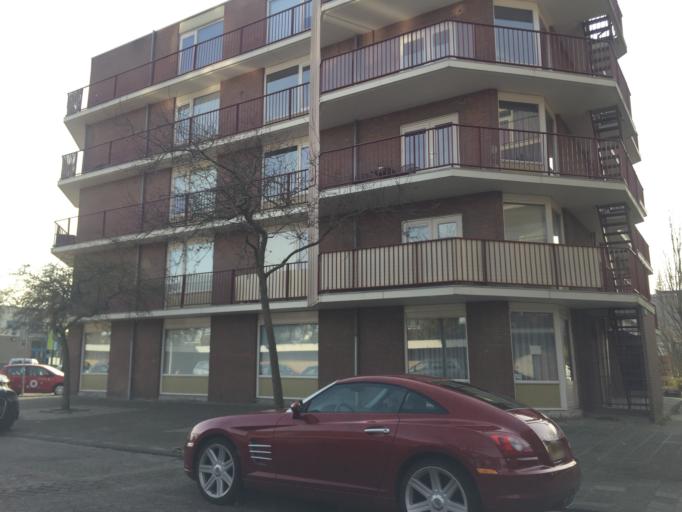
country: NL
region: South Holland
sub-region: Gemeente Leiden
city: Leiden
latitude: 52.1802
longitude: 4.5035
